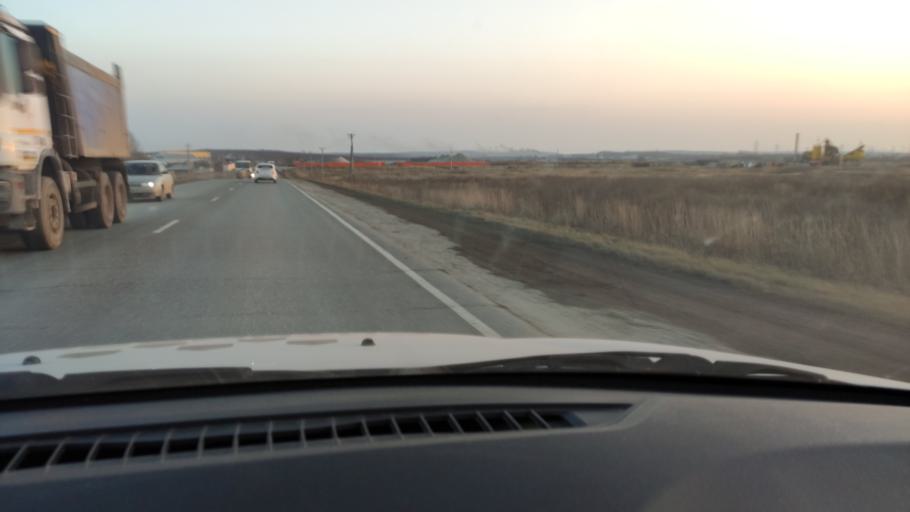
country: RU
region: Perm
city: Froly
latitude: 57.9113
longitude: 56.1919
